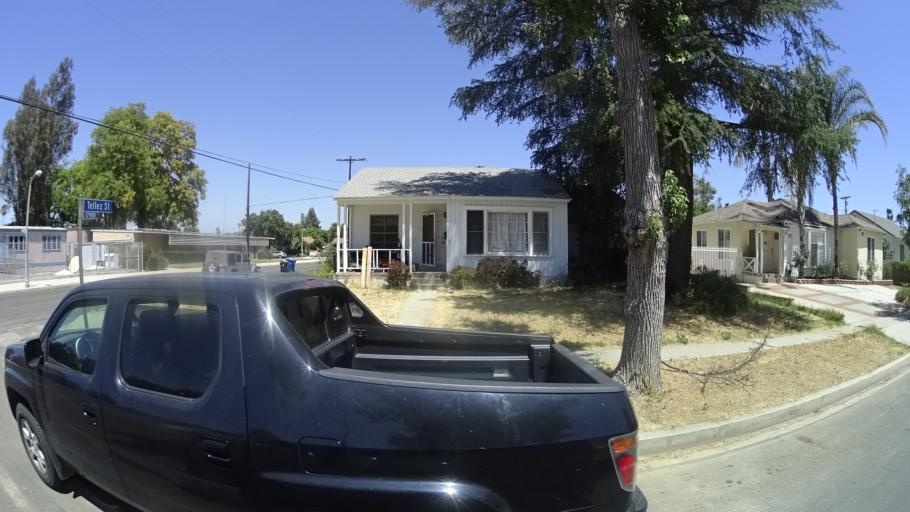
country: US
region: California
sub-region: Los Angeles County
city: Northridge
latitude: 34.1887
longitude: -118.5235
